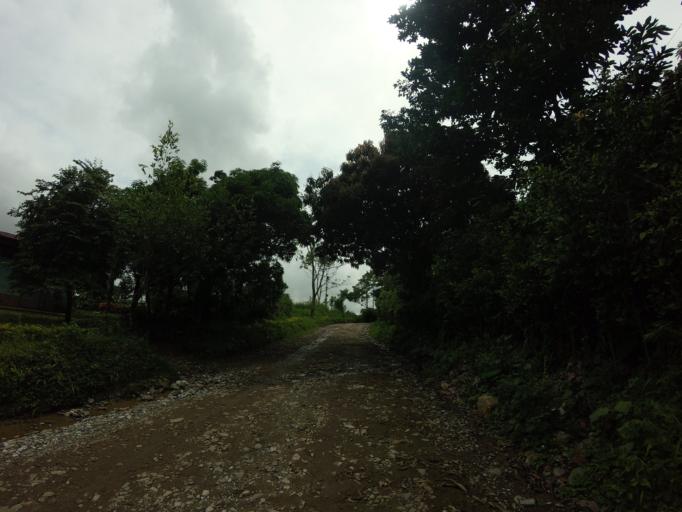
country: CO
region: Caldas
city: Victoria
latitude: 5.3068
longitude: -74.9703
